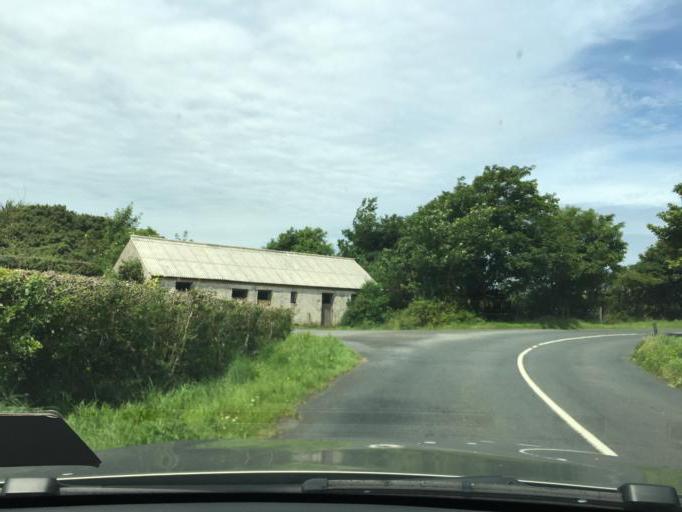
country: IE
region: Ulster
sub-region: County Donegal
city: Carndonagh
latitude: 55.3437
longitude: -7.3173
